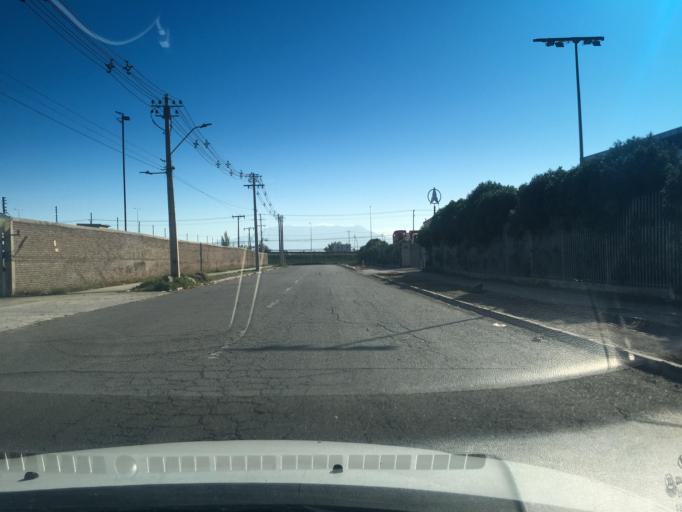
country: CL
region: Santiago Metropolitan
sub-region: Provincia de Chacabuco
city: Chicureo Abajo
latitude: -33.3100
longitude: -70.7233
